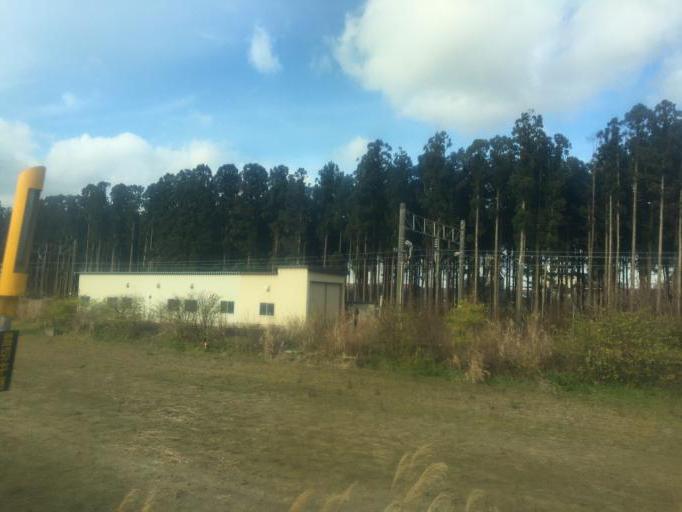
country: JP
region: Akita
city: Noshiromachi
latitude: 40.1895
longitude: 140.0606
